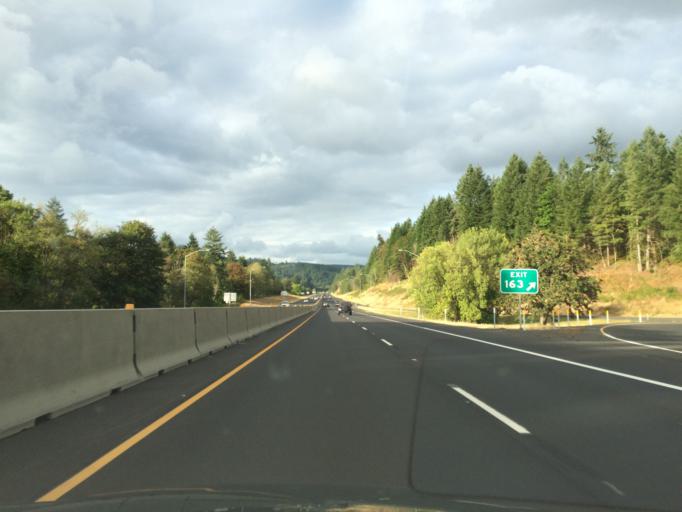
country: US
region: Oregon
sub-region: Douglas County
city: Drain
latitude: 43.7225
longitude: -123.2076
